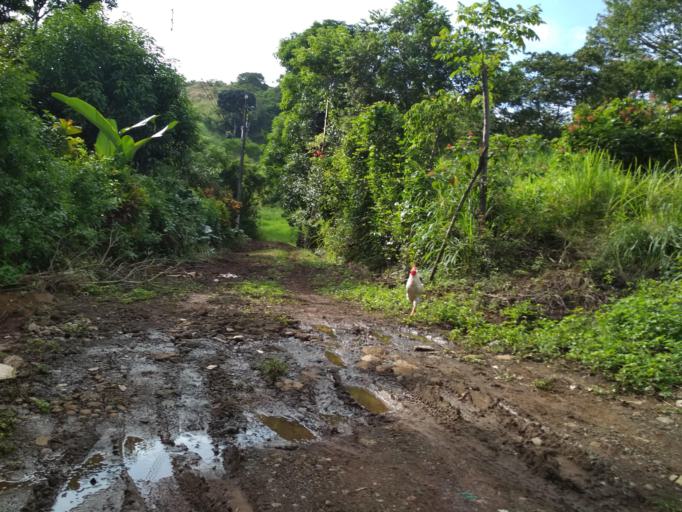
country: MX
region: Veracruz
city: Catemaco
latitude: 18.3848
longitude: -95.1254
